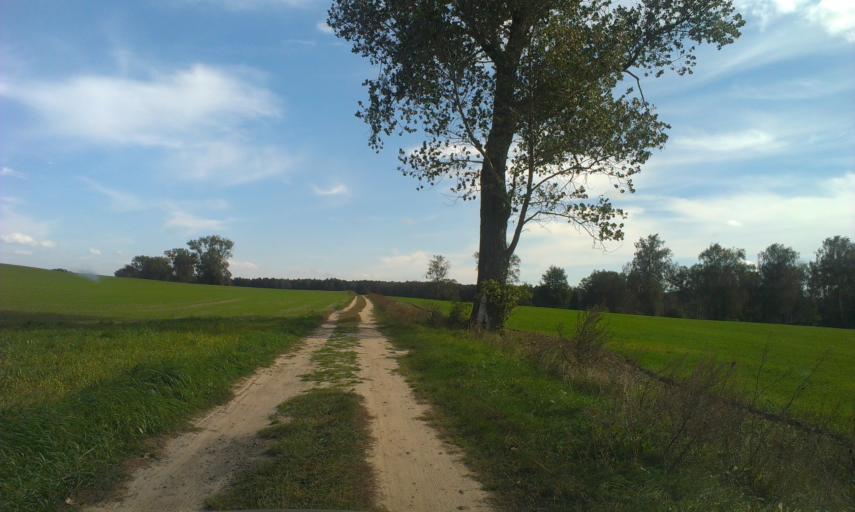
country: PL
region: Greater Poland Voivodeship
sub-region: Powiat zlotowski
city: Zakrzewo
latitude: 53.3053
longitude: 17.1505
